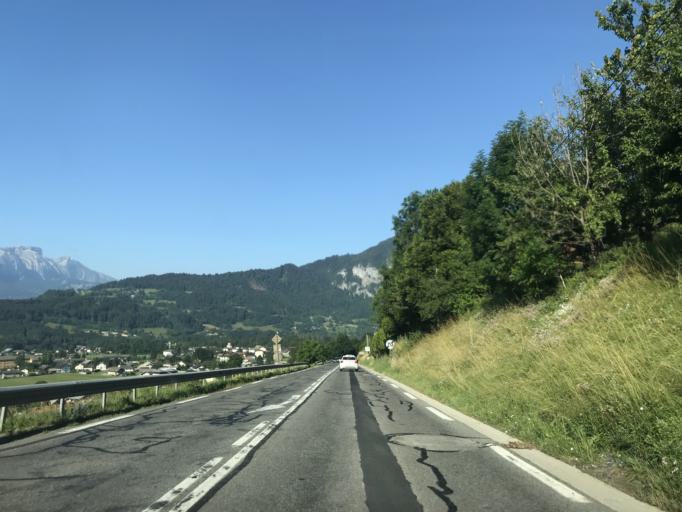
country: FR
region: Rhone-Alpes
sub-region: Departement de la Haute-Savoie
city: Taninges
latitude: 46.1097
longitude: 6.6026
